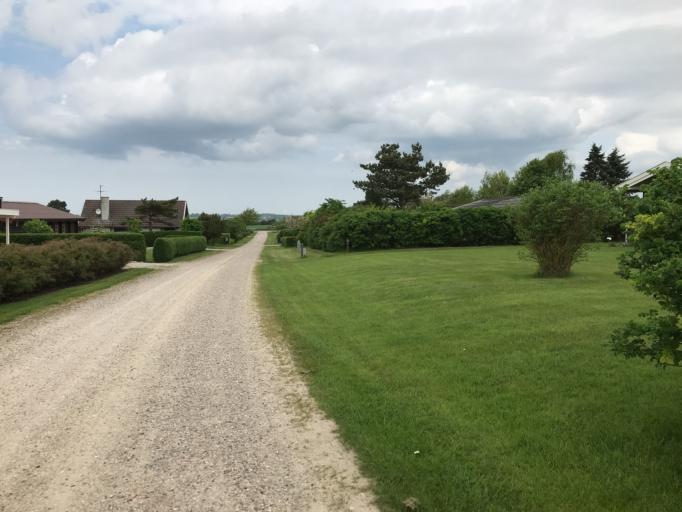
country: DK
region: South Denmark
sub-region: Assens Kommune
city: Assens
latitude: 55.3325
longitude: 9.8800
